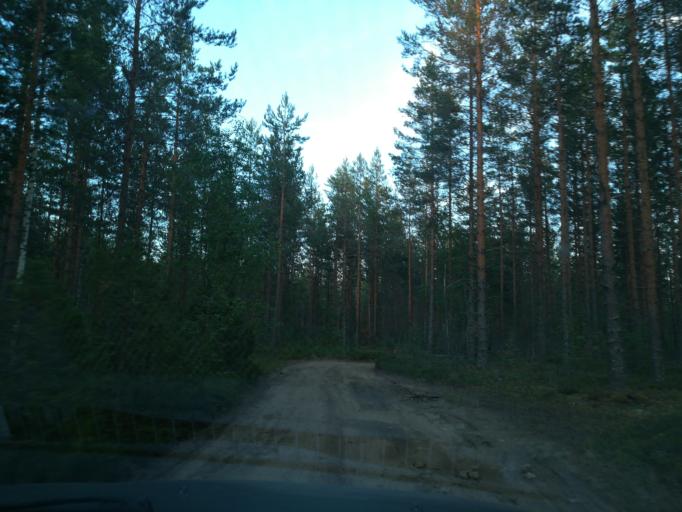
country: FI
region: South Karelia
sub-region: Lappeenranta
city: Joutseno
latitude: 61.3427
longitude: 28.4030
